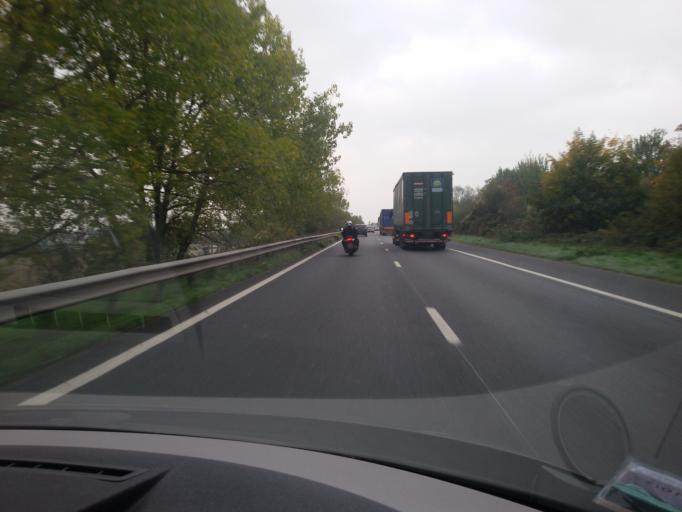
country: FR
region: Ile-de-France
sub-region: Departement de l'Essonne
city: Saclay
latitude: 48.7376
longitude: 2.1770
